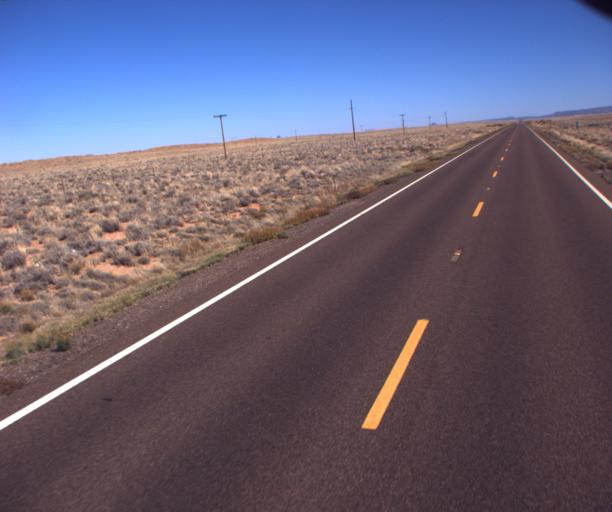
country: US
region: Arizona
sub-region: Navajo County
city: Winslow
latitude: 35.1223
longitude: -110.5069
